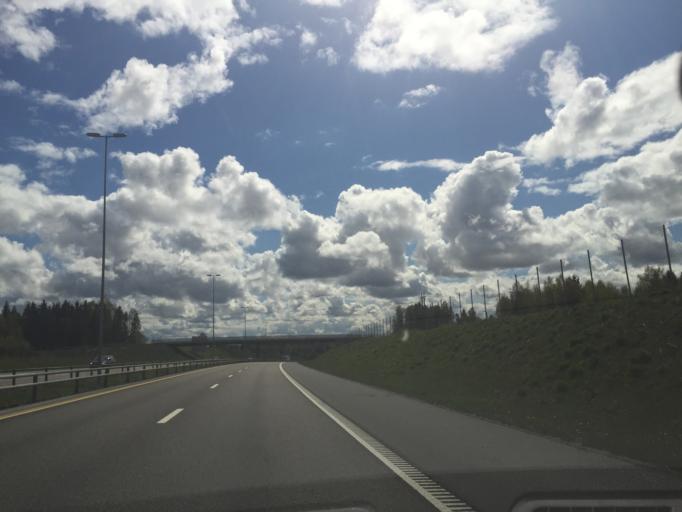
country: NO
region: Akershus
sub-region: Eidsvoll
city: Raholt
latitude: 60.2485
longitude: 11.1828
